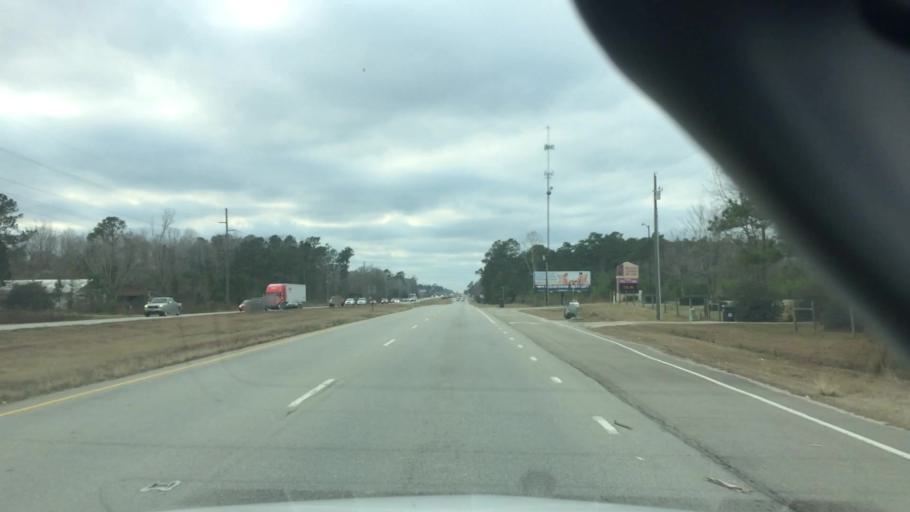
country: US
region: North Carolina
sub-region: Brunswick County
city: Sunset Beach
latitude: 33.9490
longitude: -78.4862
